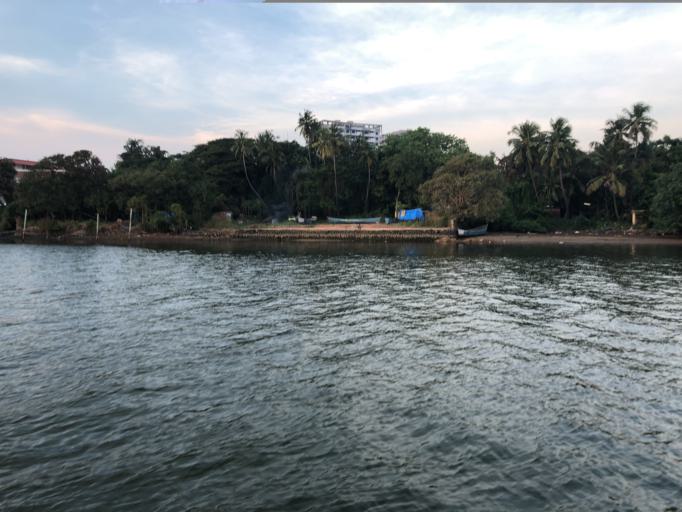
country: IN
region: Karnataka
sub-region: Dakshina Kannada
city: Ullal
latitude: 12.8417
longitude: 74.8441
